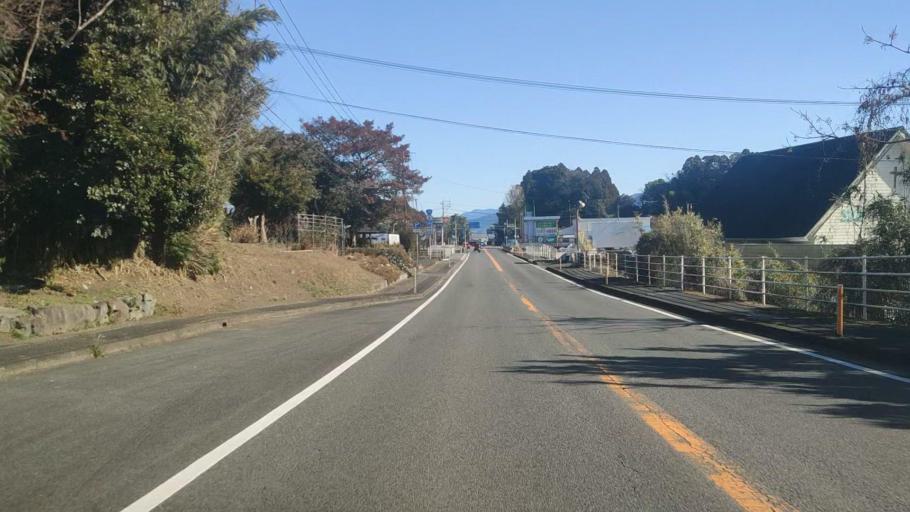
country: JP
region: Miyazaki
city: Miyakonojo
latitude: 31.7093
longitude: 131.0494
